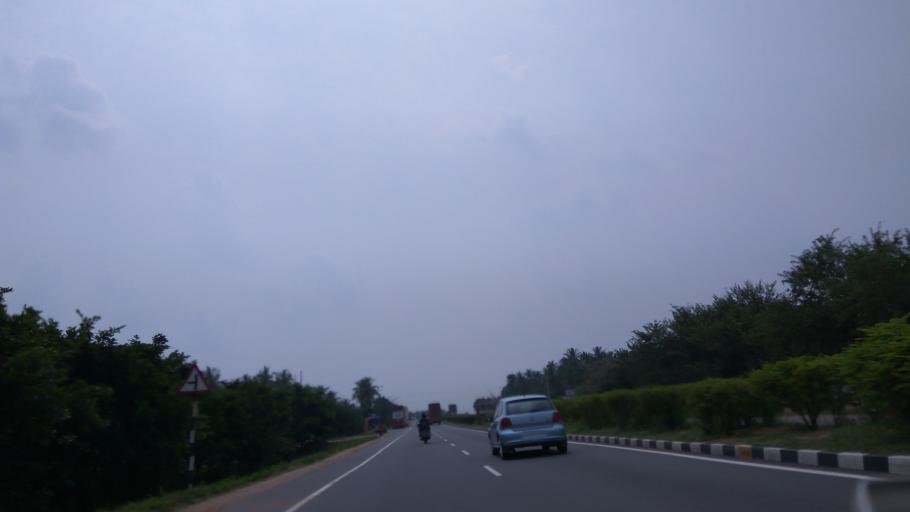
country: IN
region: Tamil Nadu
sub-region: Dharmapuri
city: Palakkodu
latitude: 12.2879
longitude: 78.1987
